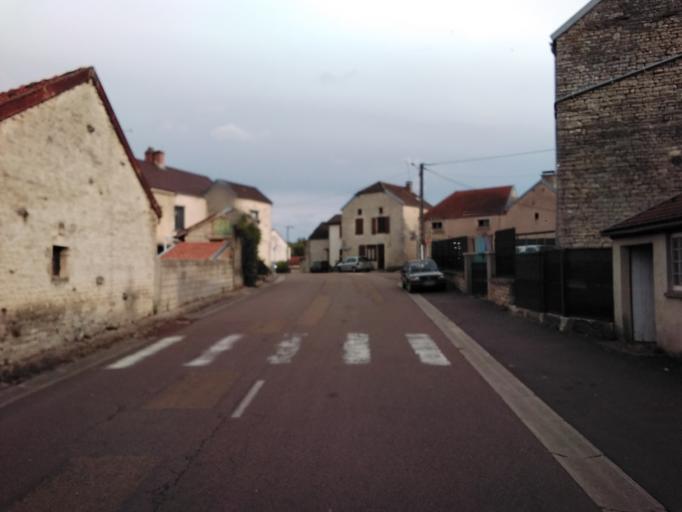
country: FR
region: Champagne-Ardenne
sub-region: Departement de l'Aube
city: Les Riceys
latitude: 47.9170
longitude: 4.3619
